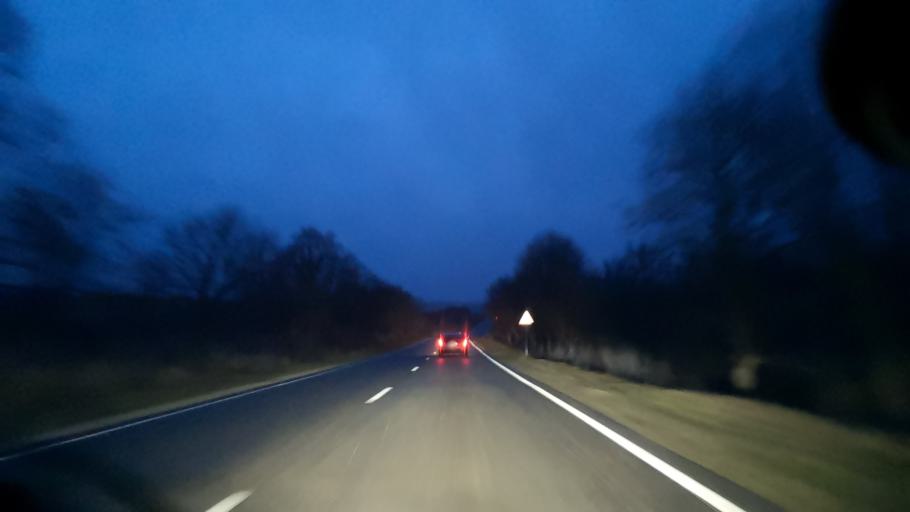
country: MD
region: Orhei
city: Orhei
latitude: 47.4826
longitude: 28.7912
